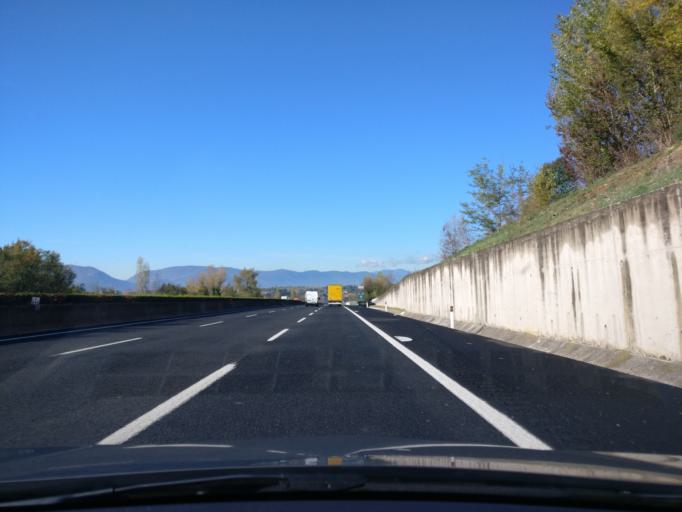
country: IT
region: Latium
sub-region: Provincia di Frosinone
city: Ceprano
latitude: 41.5436
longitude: 13.5315
